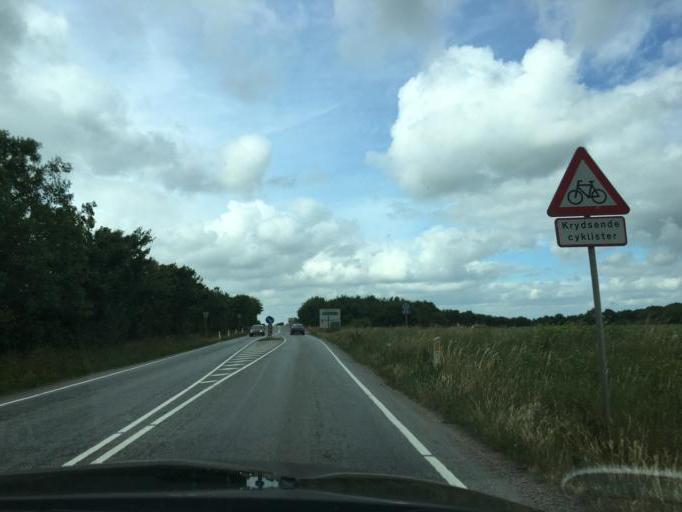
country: DK
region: South Denmark
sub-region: Esbjerg Kommune
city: Bramming
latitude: 55.5026
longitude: 8.6980
